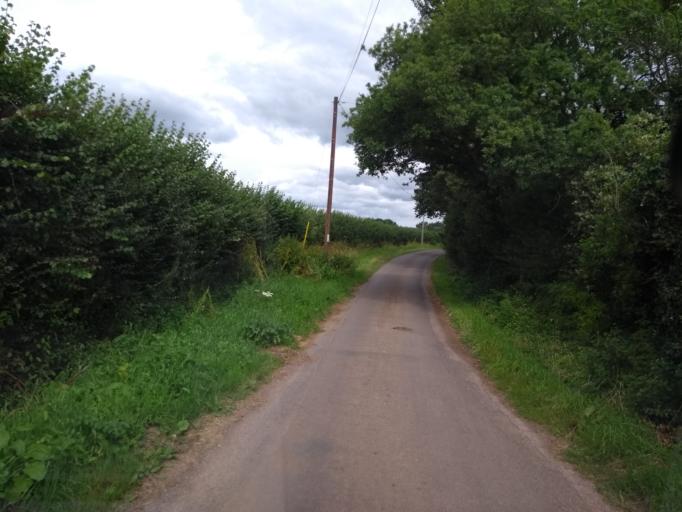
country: GB
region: England
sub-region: Somerset
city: Creech Saint Michael
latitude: 51.0360
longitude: -3.0141
